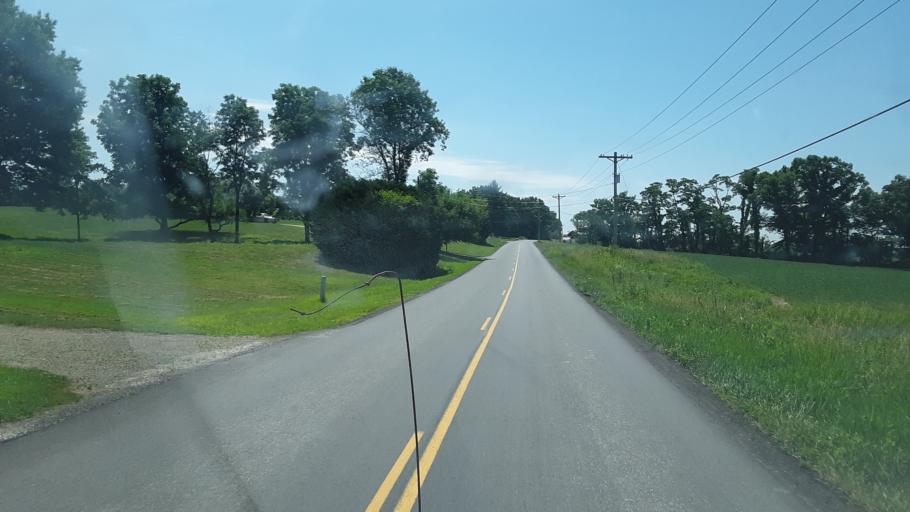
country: US
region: Ohio
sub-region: Wayne County
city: Shreve
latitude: 40.7578
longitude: -82.0766
